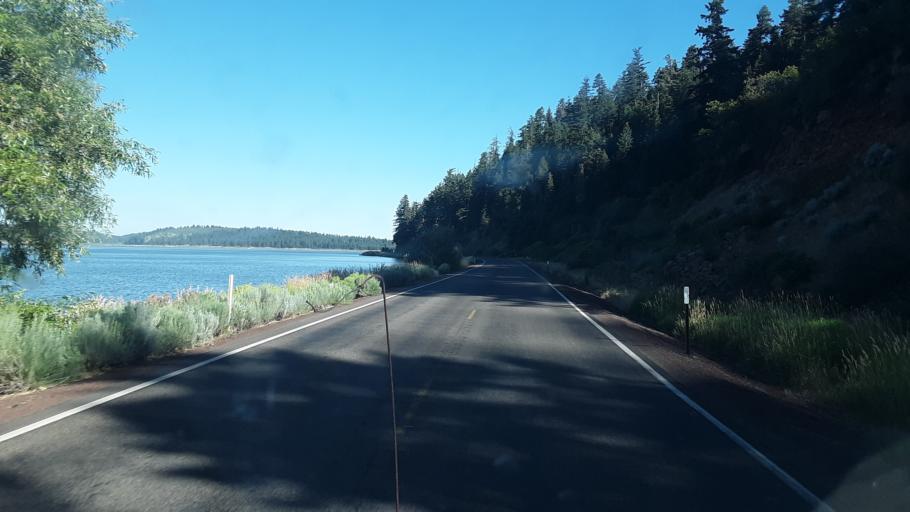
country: US
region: Oregon
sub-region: Klamath County
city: Klamath Falls
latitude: 42.3084
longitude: -121.9400
